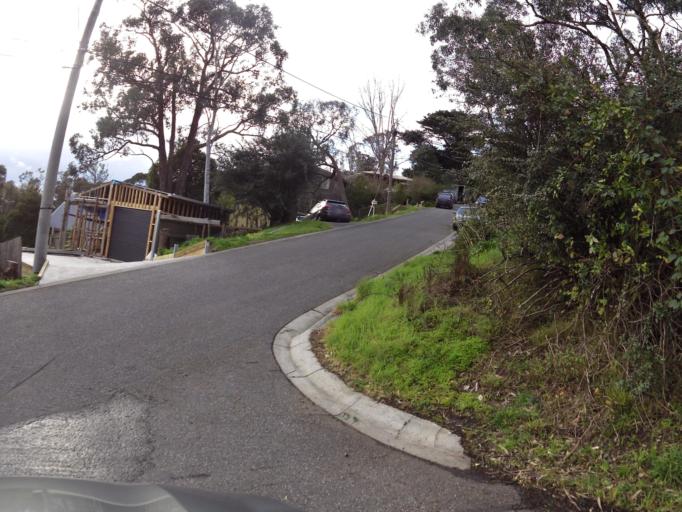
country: AU
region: Victoria
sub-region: Knox
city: Ferntree Gully
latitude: -37.8808
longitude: 145.3034
